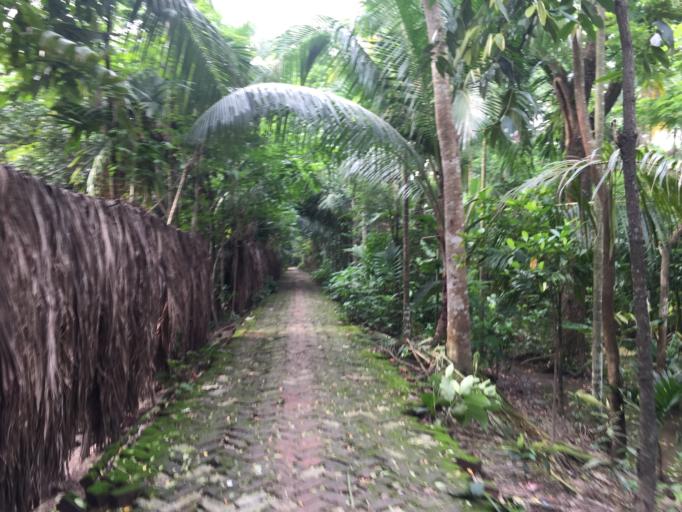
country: BD
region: Barisal
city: Mathba
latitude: 22.1907
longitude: 89.9248
